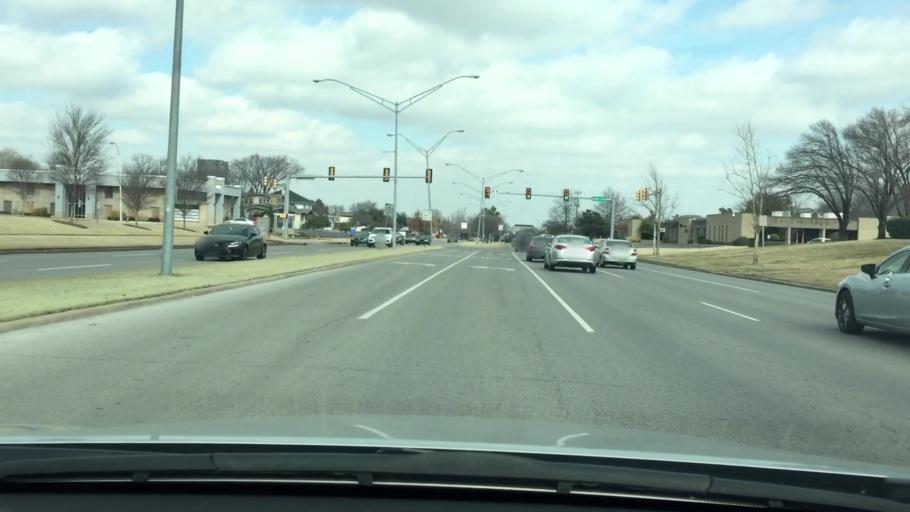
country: US
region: Oklahoma
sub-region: Oklahoma County
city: Nichols Hills
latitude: 35.5105
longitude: -97.5343
